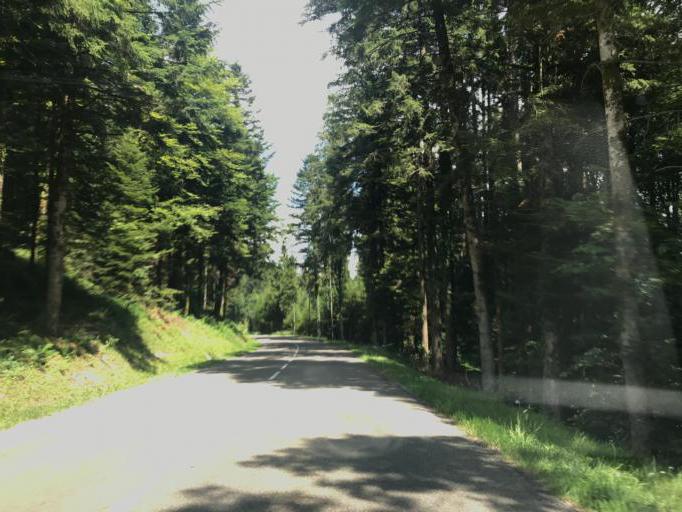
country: FR
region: Franche-Comte
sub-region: Departement du Jura
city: Clairvaux-les-Lacs
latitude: 46.5350
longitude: 5.7940
